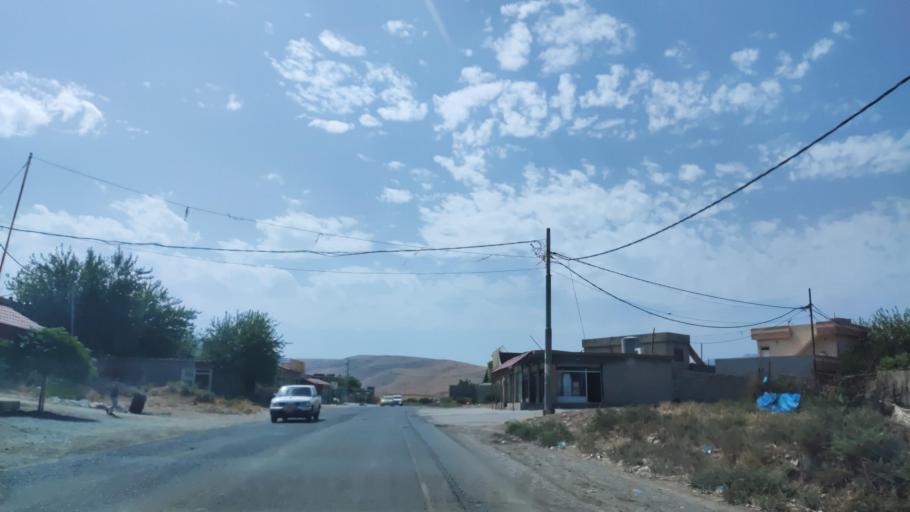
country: IQ
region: Arbil
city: Shaqlawah
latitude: 36.4869
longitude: 44.3971
